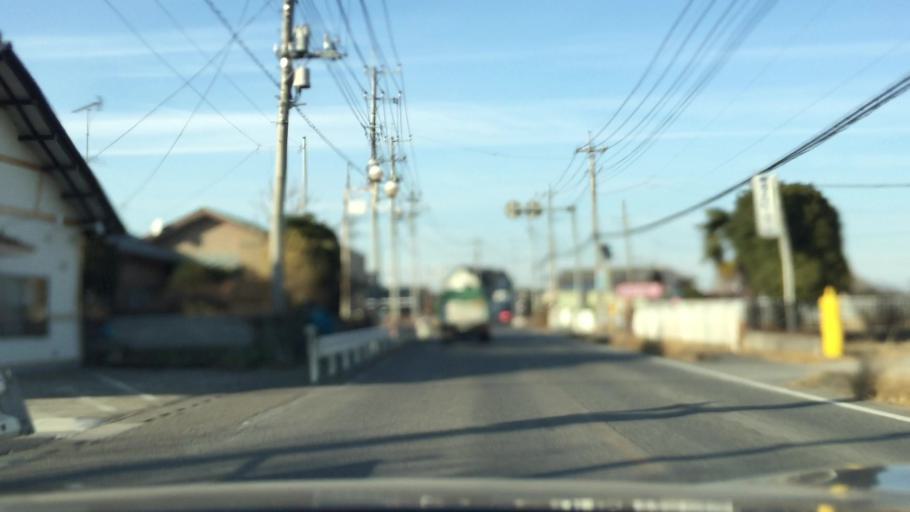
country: JP
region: Saitama
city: Menuma
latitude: 36.2035
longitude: 139.3744
